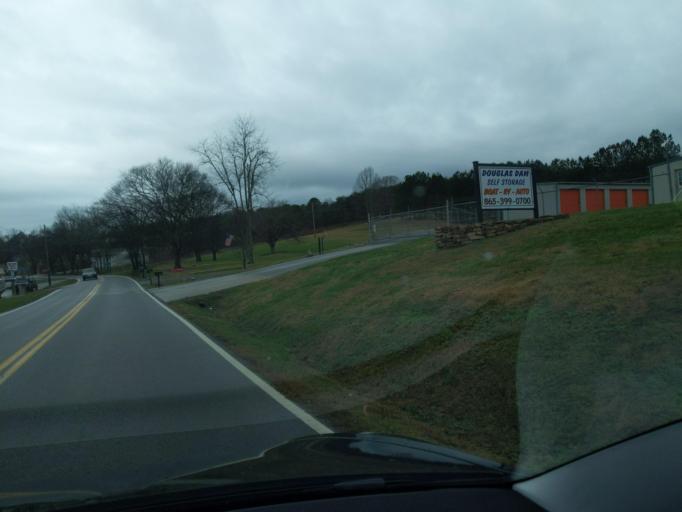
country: US
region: Tennessee
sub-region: Sevier County
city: Sevierville
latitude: 35.9730
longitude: -83.5396
